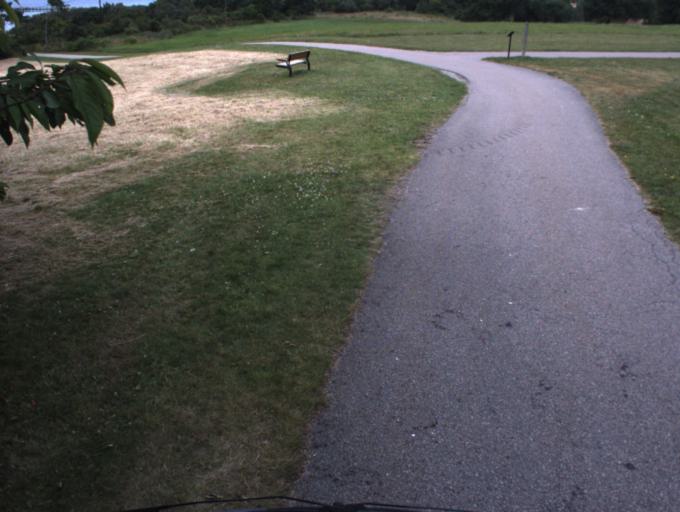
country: SE
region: Skane
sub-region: Helsingborg
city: Rydeback
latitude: 55.9629
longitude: 12.7597
